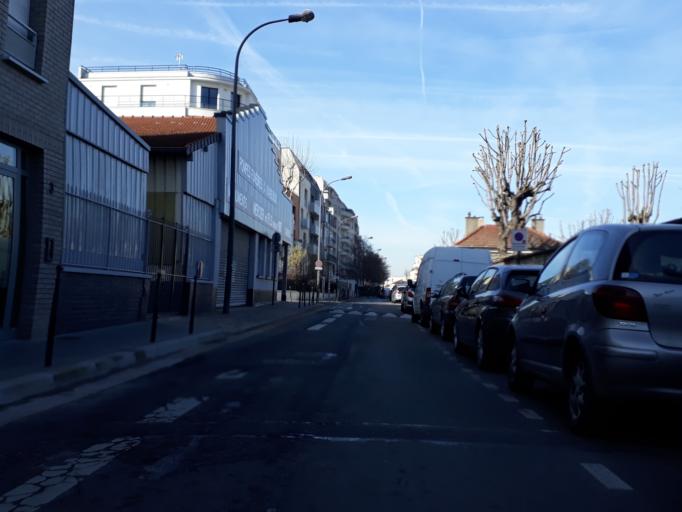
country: FR
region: Ile-de-France
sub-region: Departement des Hauts-de-Seine
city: Asnieres-sur-Seine
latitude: 48.9168
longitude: 2.2890
